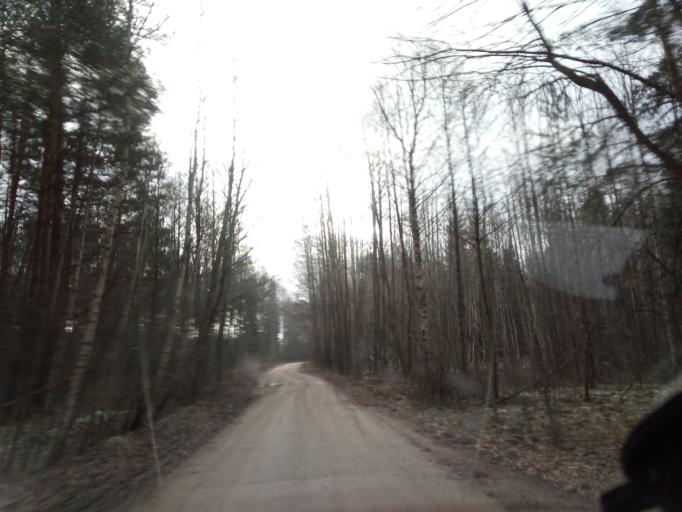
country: LT
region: Alytaus apskritis
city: Varena
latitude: 53.9941
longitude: 24.3475
